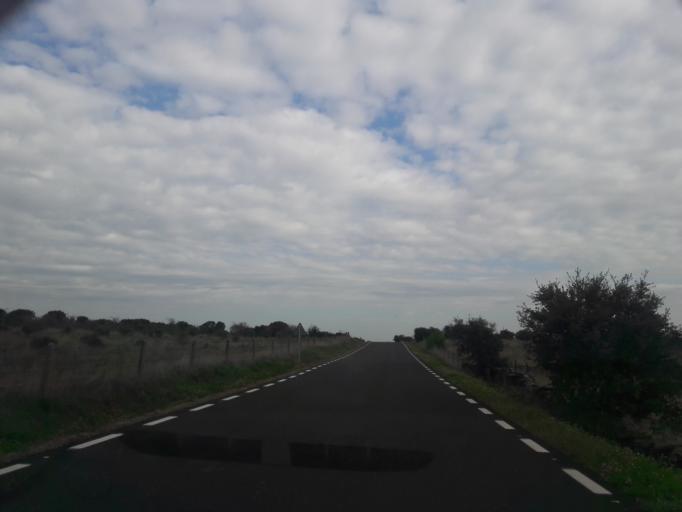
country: ES
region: Castille and Leon
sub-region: Provincia de Salamanca
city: Pastores
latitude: 40.5098
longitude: -6.5287
